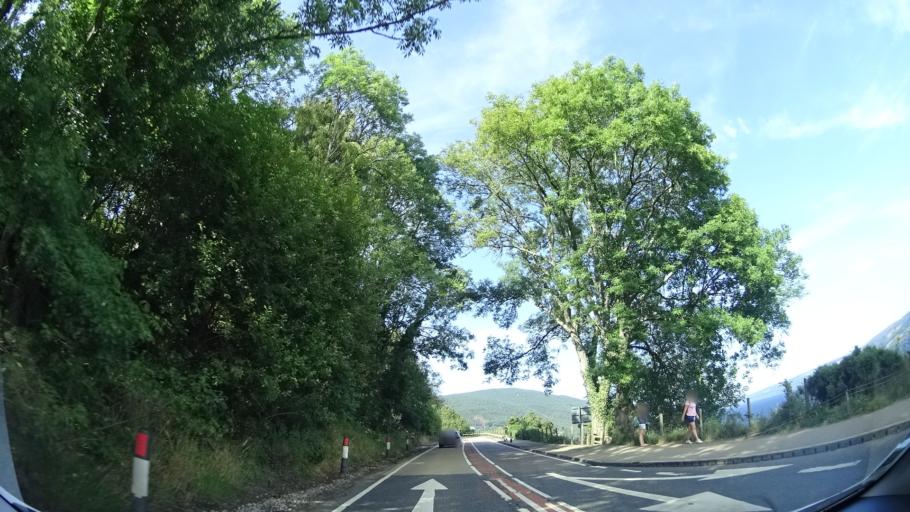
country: GB
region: Scotland
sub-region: Highland
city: Beauly
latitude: 57.3256
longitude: -4.4454
